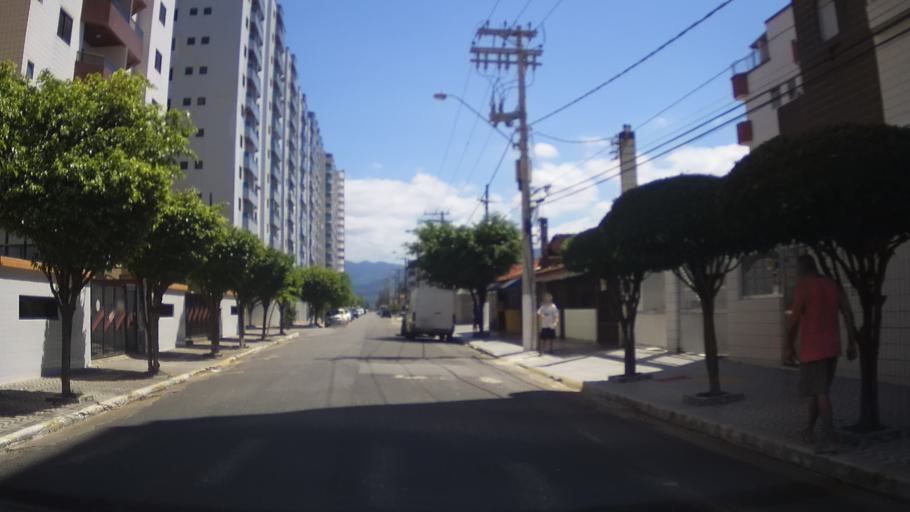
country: BR
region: Sao Paulo
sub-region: Praia Grande
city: Praia Grande
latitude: -24.0259
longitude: -46.4705
